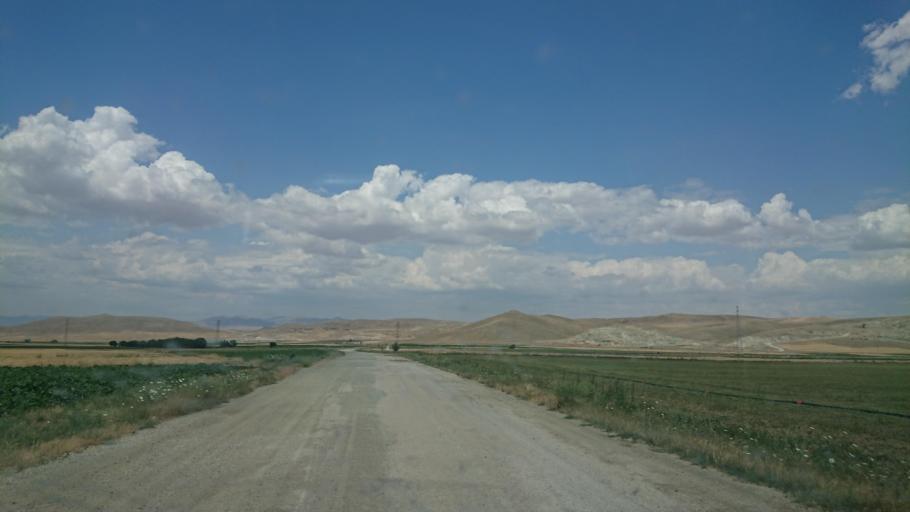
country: TR
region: Aksaray
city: Sariyahsi
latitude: 38.9772
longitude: 33.9015
